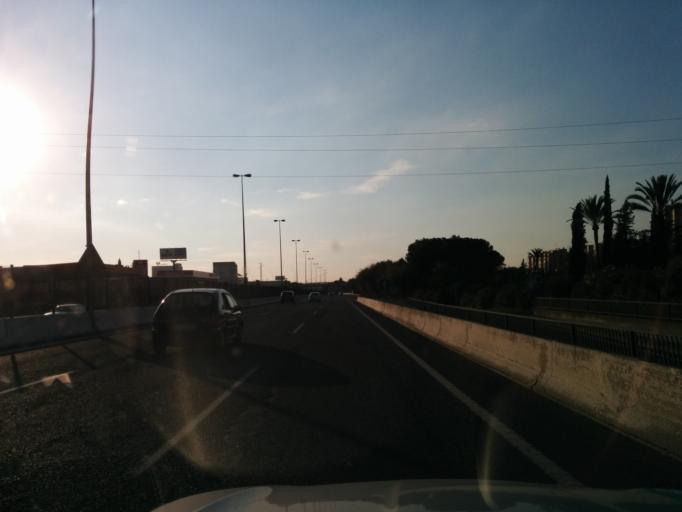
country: ES
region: Andalusia
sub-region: Provincia de Sevilla
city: Sevilla
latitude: 37.3860
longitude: -5.9194
